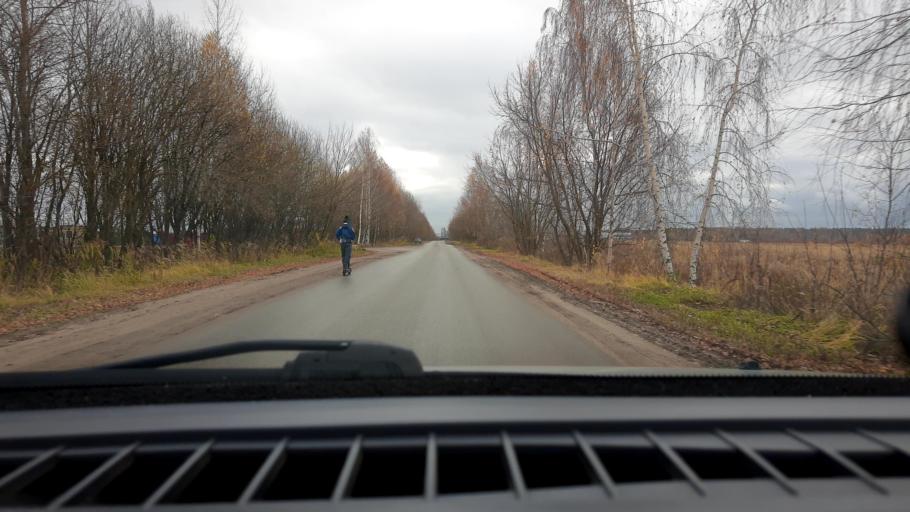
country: RU
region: Nizjnij Novgorod
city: Afonino
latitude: 56.1997
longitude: 44.1334
